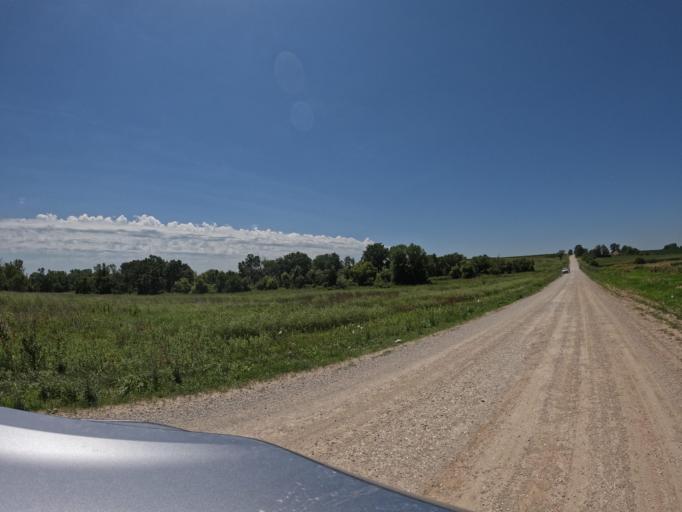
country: US
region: Iowa
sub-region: Keokuk County
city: Sigourney
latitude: 41.4089
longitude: -92.3310
